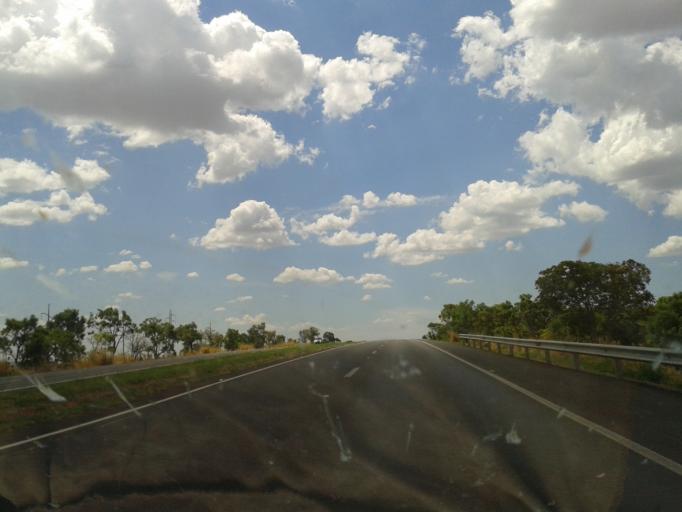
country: BR
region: Minas Gerais
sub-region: Uberlandia
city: Uberlandia
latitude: -19.1021
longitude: -48.1808
